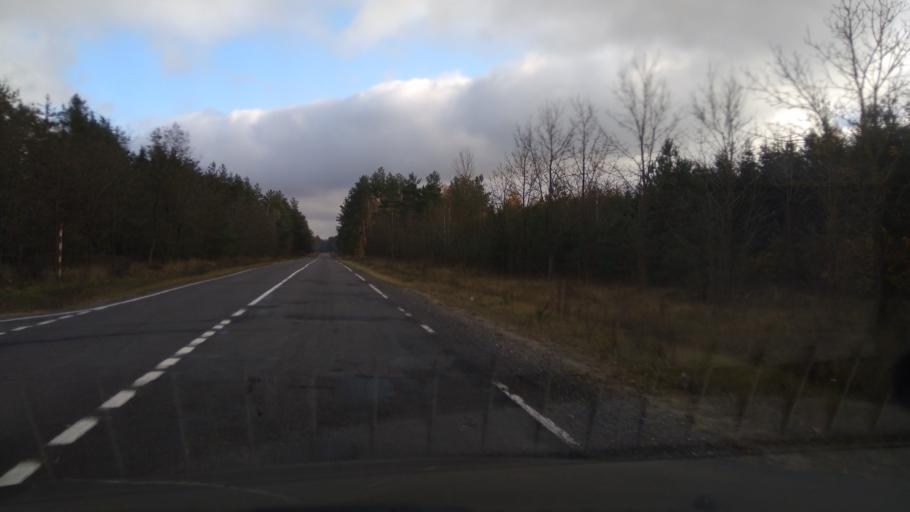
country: BY
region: Minsk
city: Slutsk
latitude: 53.2292
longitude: 27.7123
